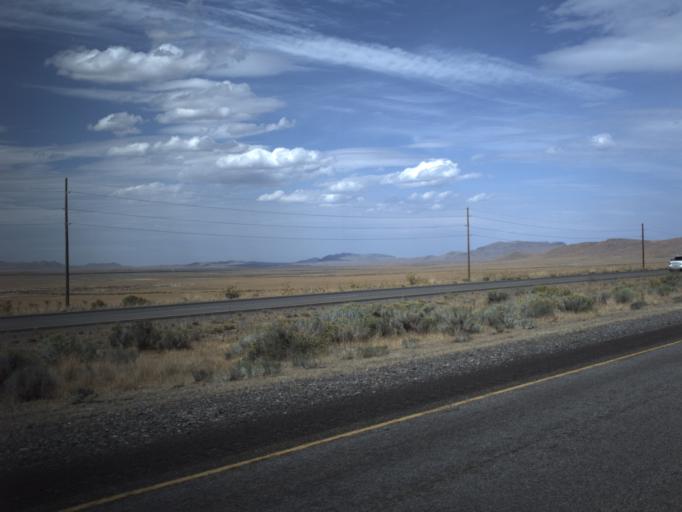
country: US
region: Utah
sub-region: Tooele County
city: Grantsville
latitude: 40.8044
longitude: -112.9375
